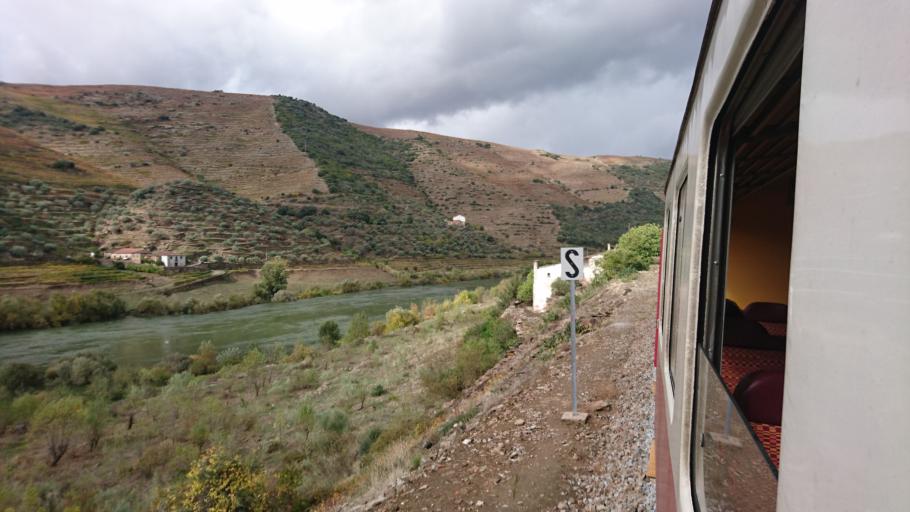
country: PT
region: Viseu
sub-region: Sao Joao da Pesqueira
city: Sao Joao da Pesqueira
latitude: 41.1753
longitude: -7.3758
